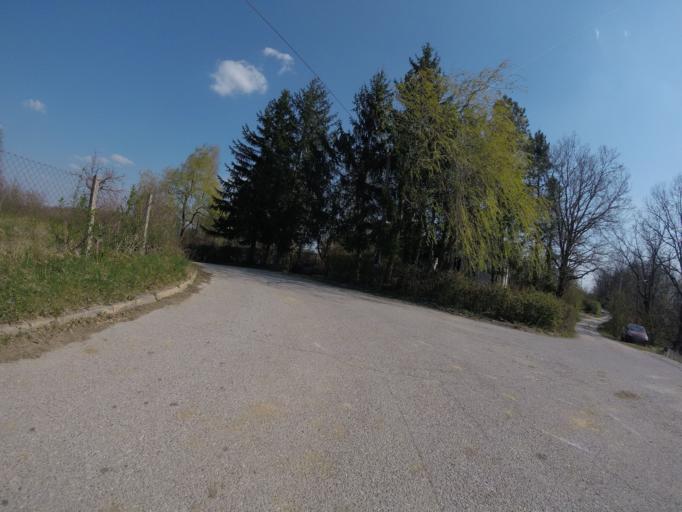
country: HR
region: Sisacko-Moslavacka
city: Gvozd
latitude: 45.5132
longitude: 15.9236
